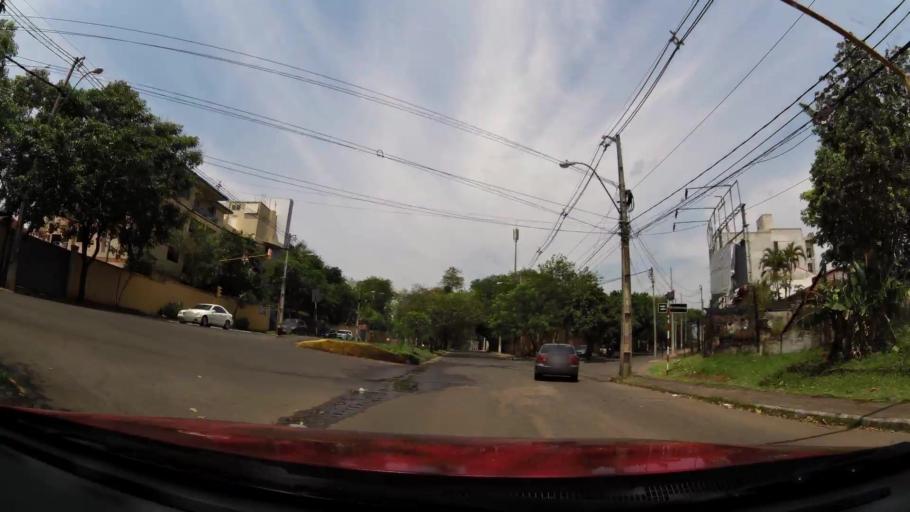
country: PY
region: Central
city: Fernando de la Mora
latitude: -25.3050
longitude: -57.5648
